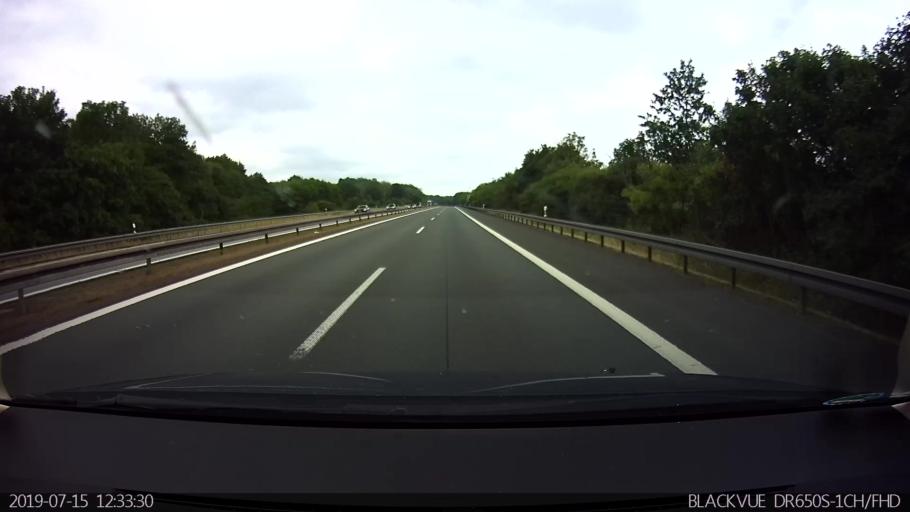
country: DE
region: Saxony
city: Bosenbrunn
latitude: 50.4341
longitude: 12.1273
